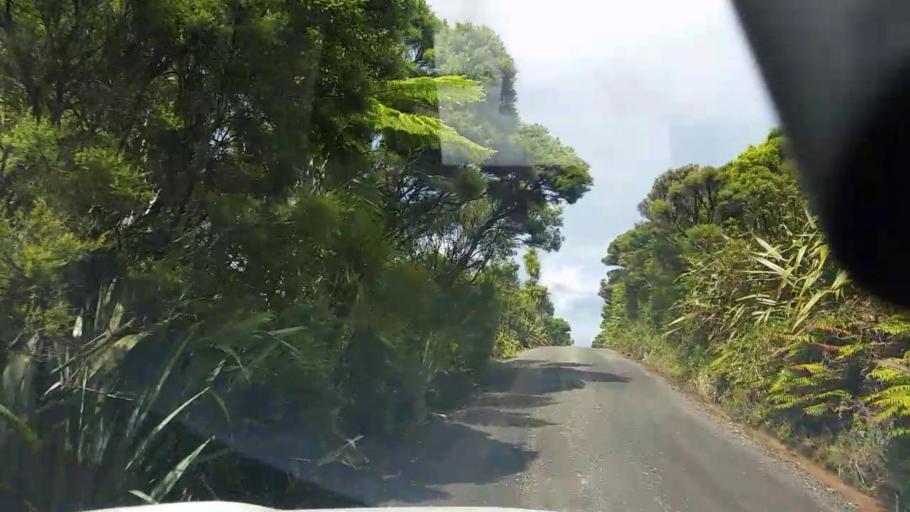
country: NZ
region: Auckland
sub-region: Auckland
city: Muriwai Beach
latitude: -36.9267
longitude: 174.4797
